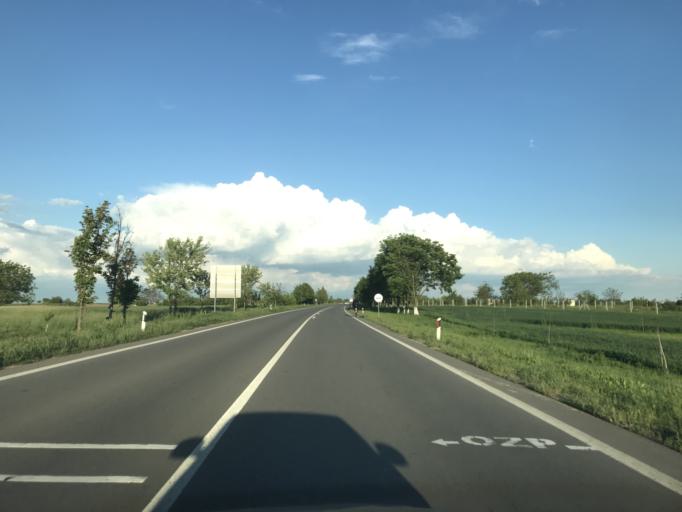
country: RS
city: Aradac
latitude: 45.3914
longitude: 20.3002
